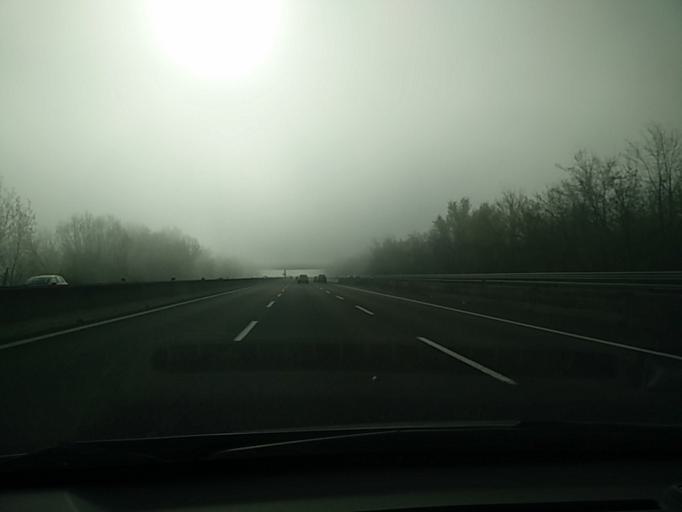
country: IT
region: Emilia-Romagna
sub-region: Provincia di Bologna
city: Villanova
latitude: 44.4775
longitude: 11.4543
